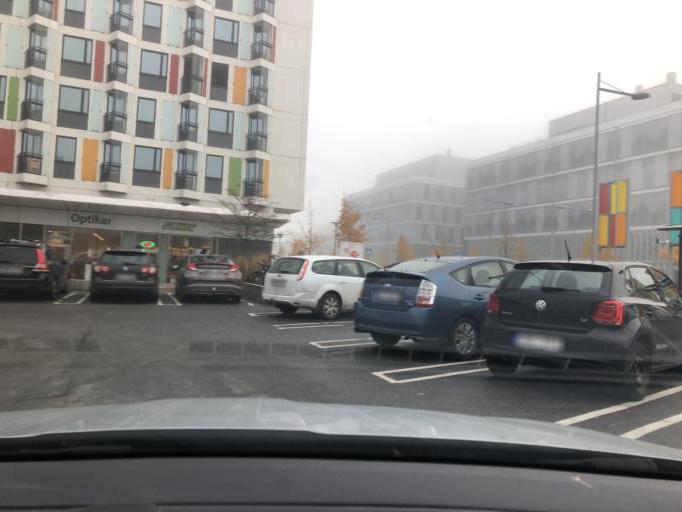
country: SE
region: Stockholm
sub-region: Botkyrka Kommun
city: Tullinge
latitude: 59.2228
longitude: 17.9382
